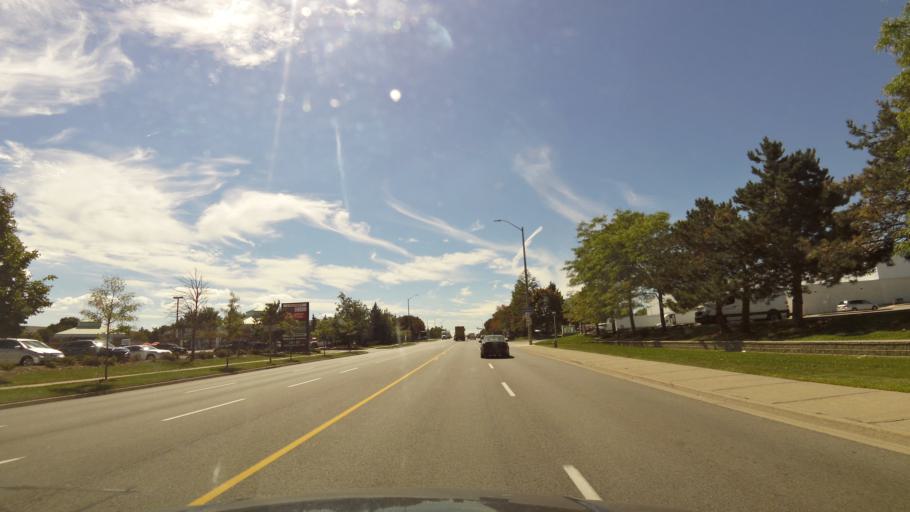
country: CA
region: Ontario
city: Mississauga
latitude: 43.6212
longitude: -79.6679
